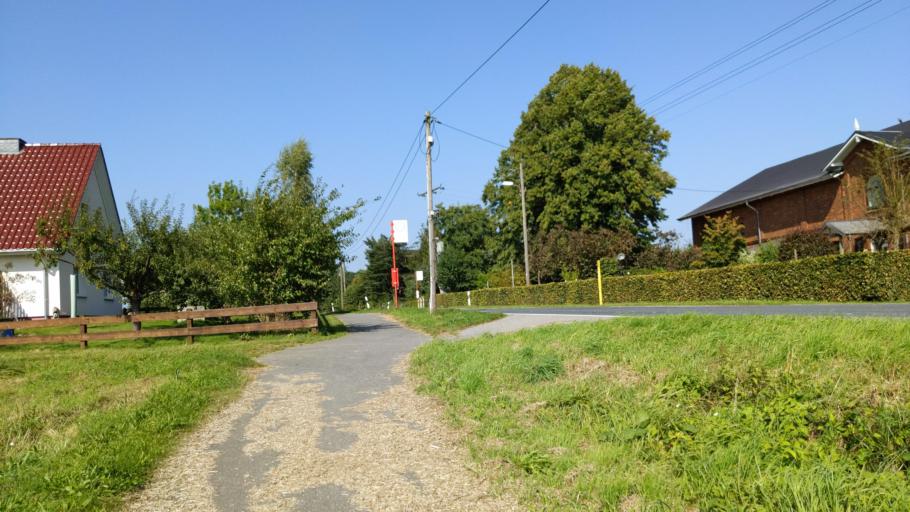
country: DE
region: Schleswig-Holstein
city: Klein Wesenberg
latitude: 53.8060
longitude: 10.5486
